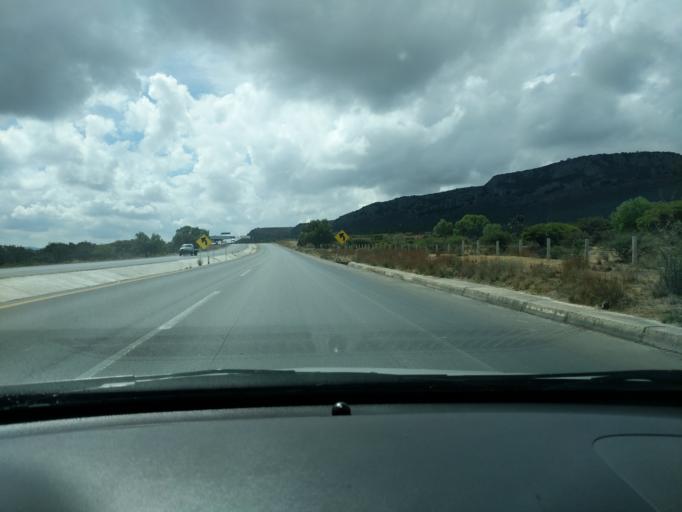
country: MX
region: Zacatecas
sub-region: Pinos
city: Santiago
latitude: 22.4033
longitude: -101.3841
